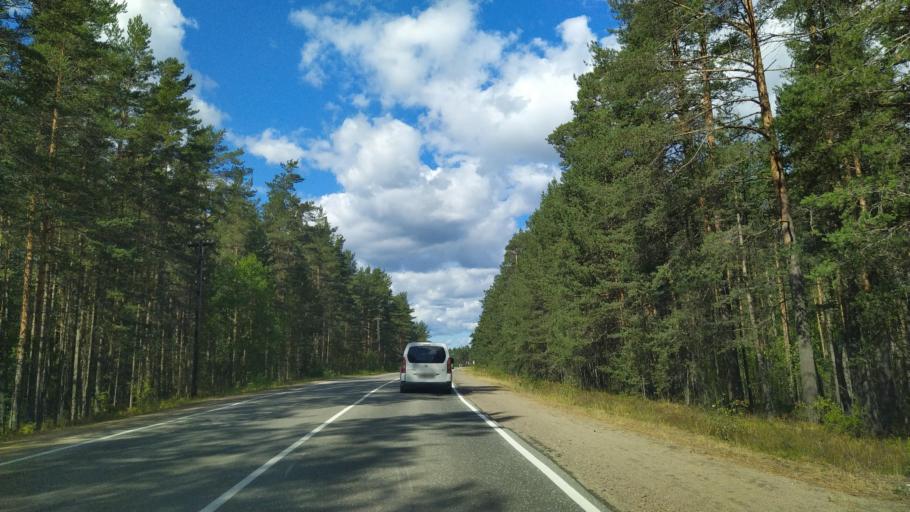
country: RU
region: Leningrad
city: Priozersk
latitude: 61.0020
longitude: 30.1961
